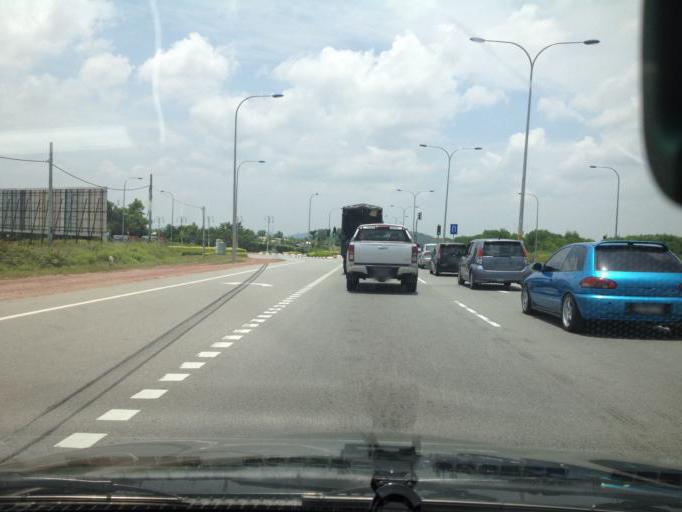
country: MY
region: Kedah
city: Sungai Petani
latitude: 5.6179
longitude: 100.5513
